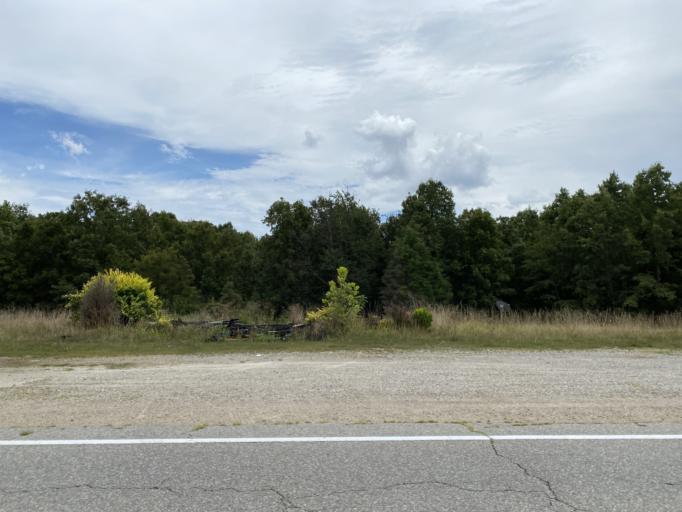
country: US
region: Arkansas
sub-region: Fulton County
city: Salem
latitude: 36.4295
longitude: -91.6998
